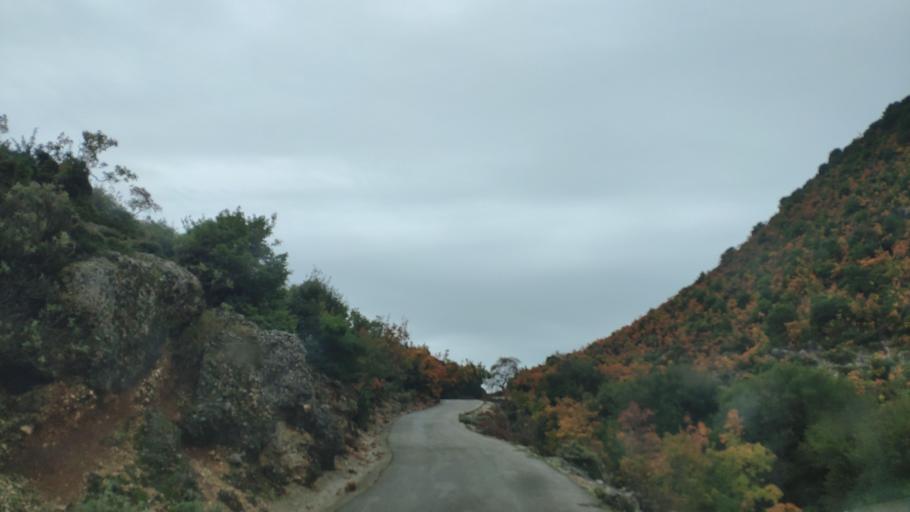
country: GR
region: Epirus
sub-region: Nomos Prevezis
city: Kanalaki
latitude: 39.3390
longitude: 20.6530
